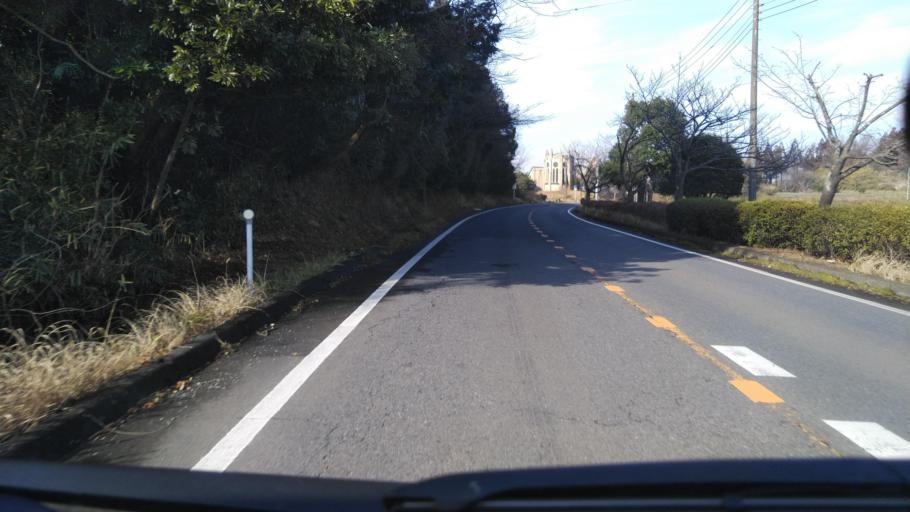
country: JP
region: Chiba
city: Katori-shi
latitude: 35.8927
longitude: 140.5243
